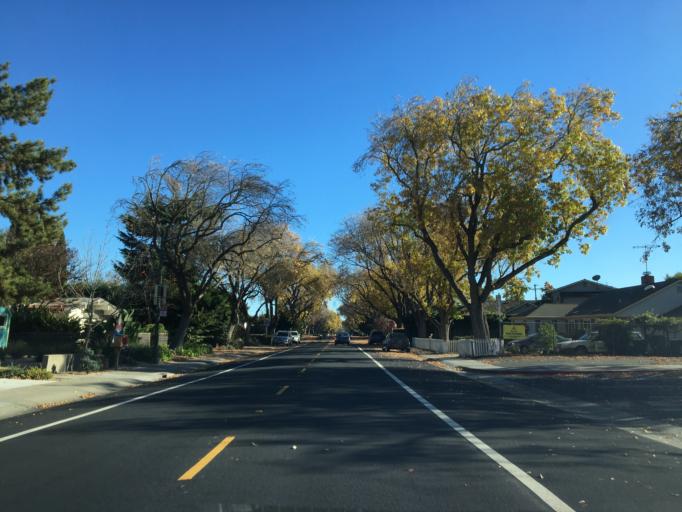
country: US
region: California
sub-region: Santa Clara County
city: Palo Alto
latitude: 37.4312
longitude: -122.1135
